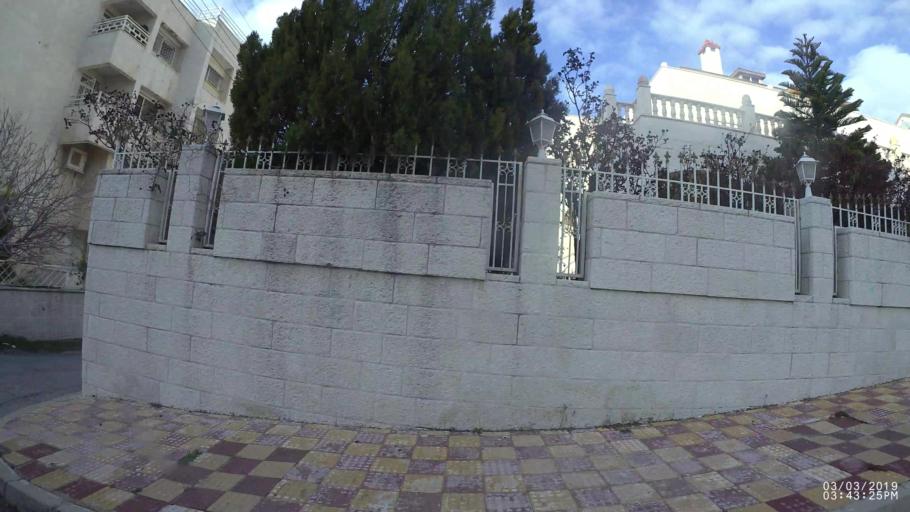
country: JO
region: Amman
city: Al Jubayhah
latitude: 31.9836
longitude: 35.8793
